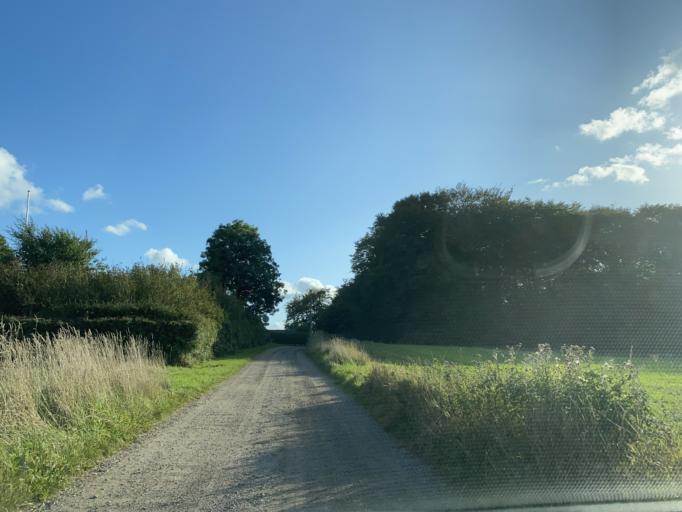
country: DK
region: Central Jutland
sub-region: Skanderborg Kommune
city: Ry
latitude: 56.1521
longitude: 9.7825
